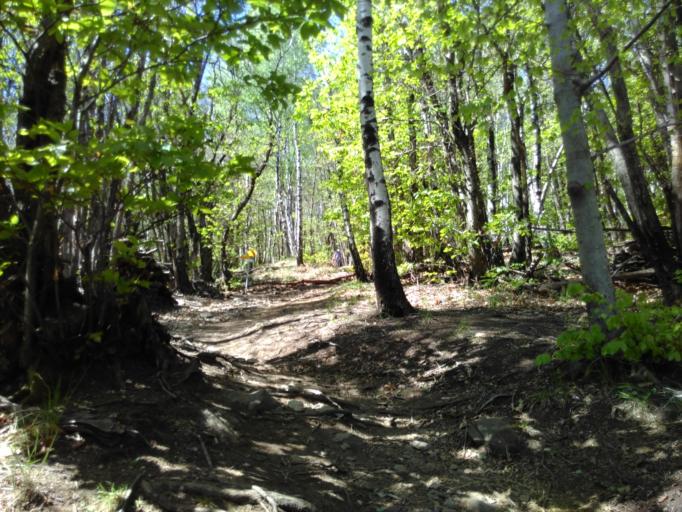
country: CH
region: Ticino
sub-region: Bellinzona District
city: Sementina
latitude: 46.1895
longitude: 8.9777
